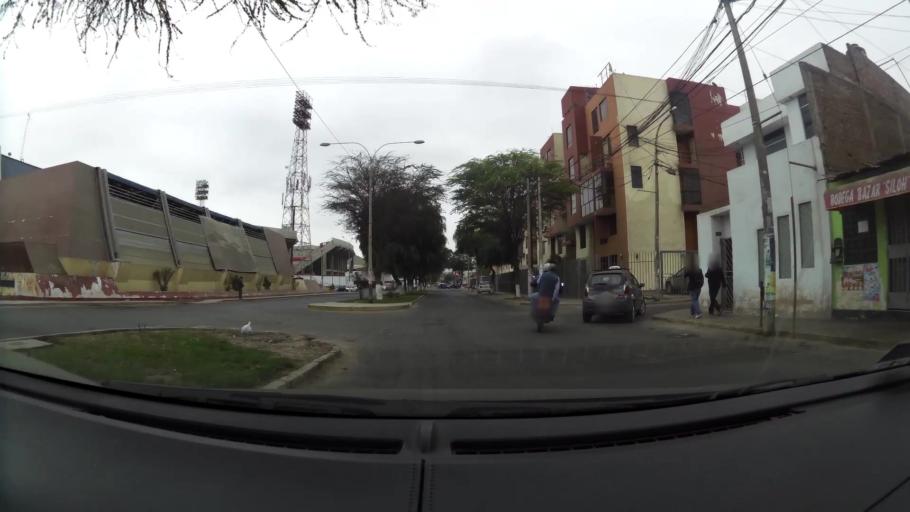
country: PE
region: La Libertad
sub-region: Provincia de Trujillo
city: Trujillo
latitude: -8.1059
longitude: -79.0294
